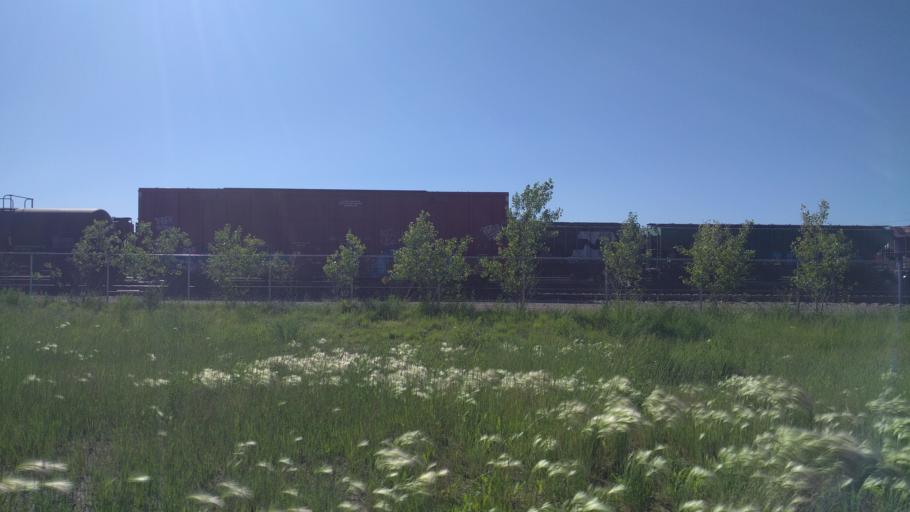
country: CA
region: Manitoba
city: Winnipeg
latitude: 49.8622
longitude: -97.1459
